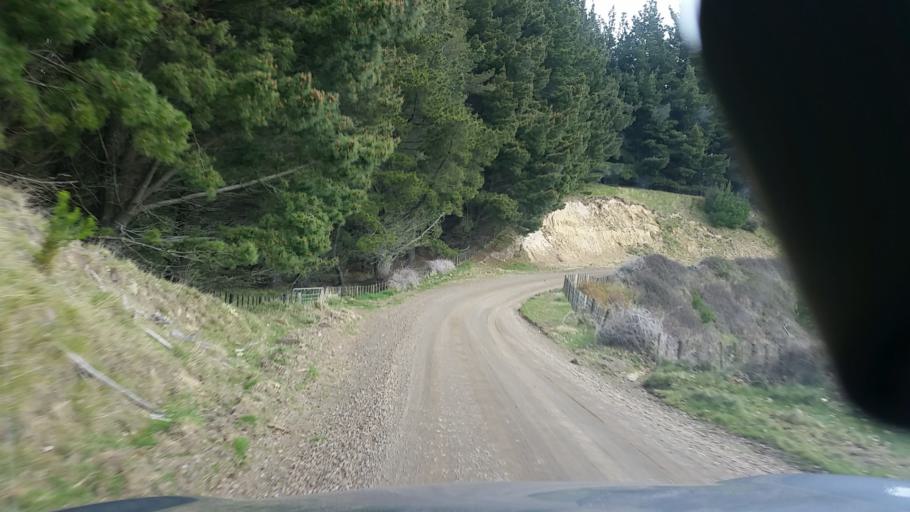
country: NZ
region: Hawke's Bay
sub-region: Napier City
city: Napier
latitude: -39.2287
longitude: 176.9851
